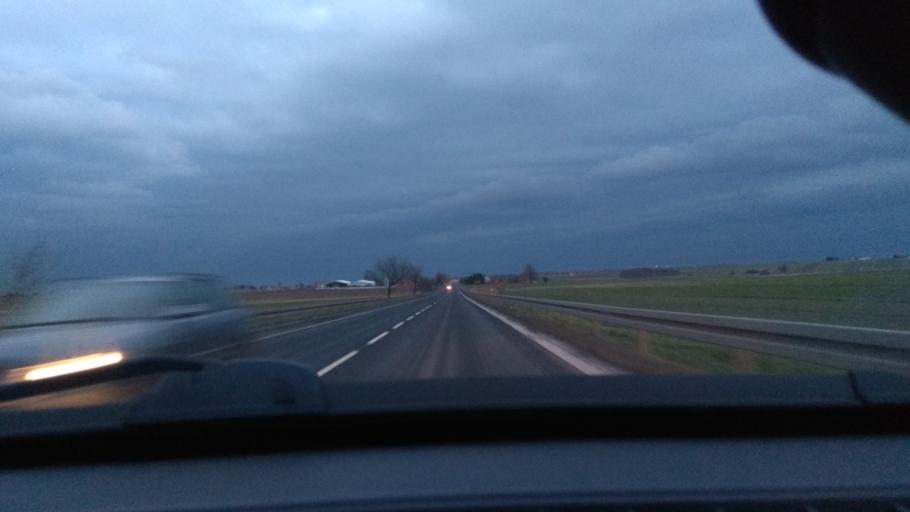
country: PL
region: Greater Poland Voivodeship
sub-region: Powiat kepinski
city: Slupia pod Kepnem
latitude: 51.2970
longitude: 18.0583
